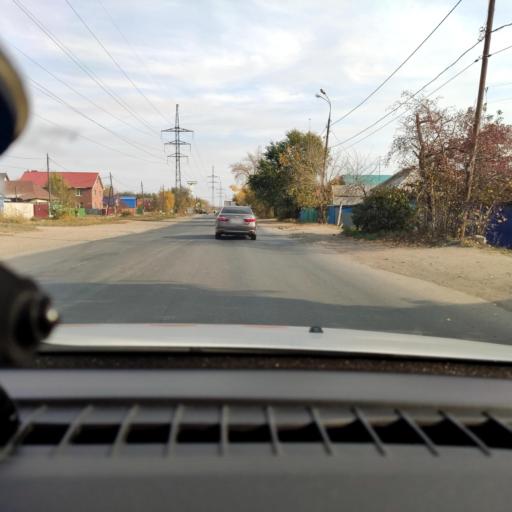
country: RU
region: Samara
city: Samara
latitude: 53.1326
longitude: 50.1285
